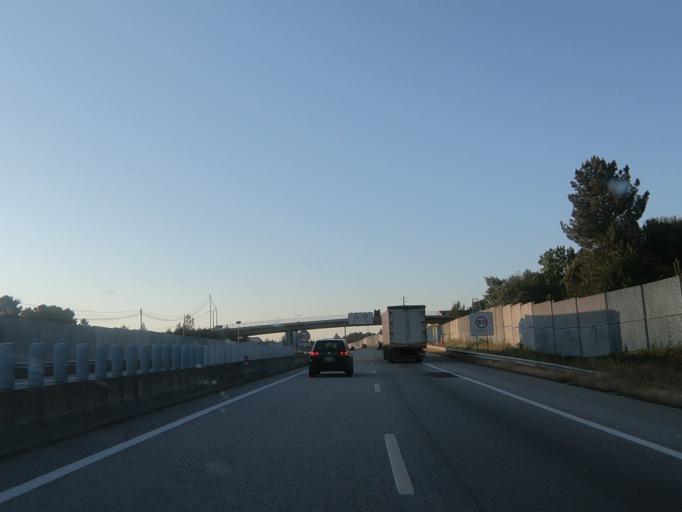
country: PT
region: Viseu
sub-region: Viseu
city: Rio de Loba
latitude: 40.6468
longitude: -7.8607
